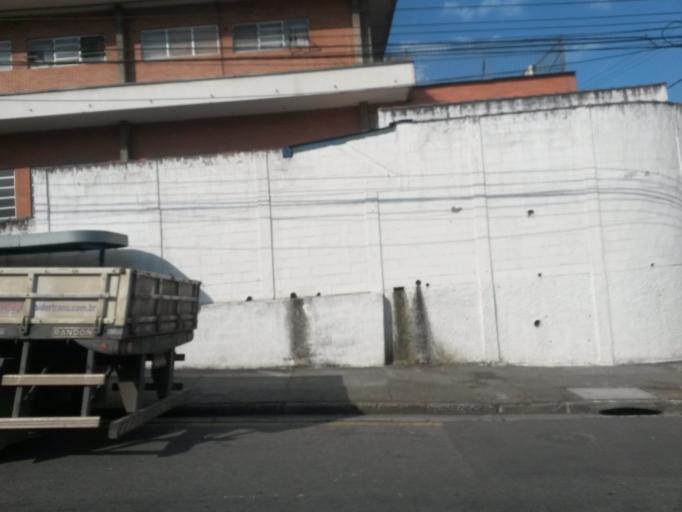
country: BR
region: Sao Paulo
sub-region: Sao Bernardo Do Campo
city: Sao Bernardo do Campo
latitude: -23.7171
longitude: -46.5621
